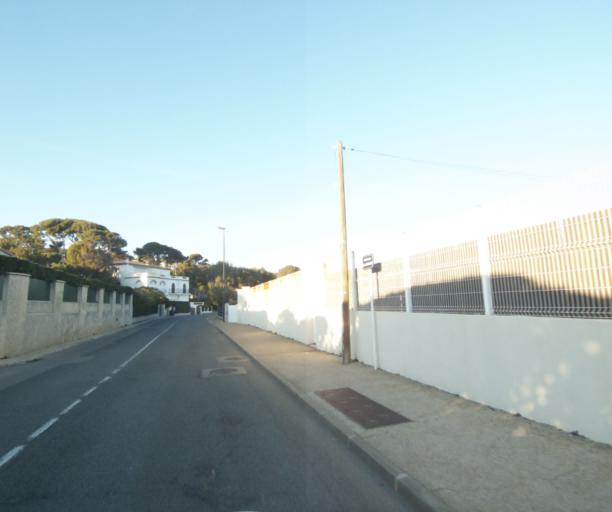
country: FR
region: Provence-Alpes-Cote d'Azur
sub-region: Departement des Alpes-Maritimes
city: Antibes
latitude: 43.5573
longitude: 7.1348
